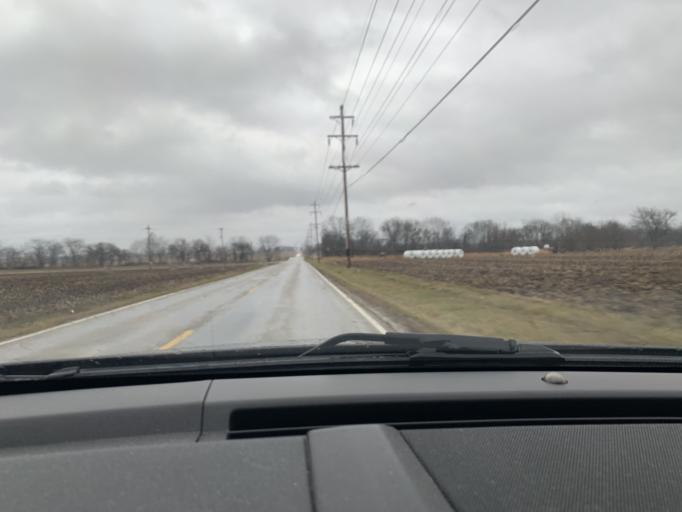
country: US
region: Ohio
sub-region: Ross County
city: Kingston
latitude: 39.4744
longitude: -82.8717
